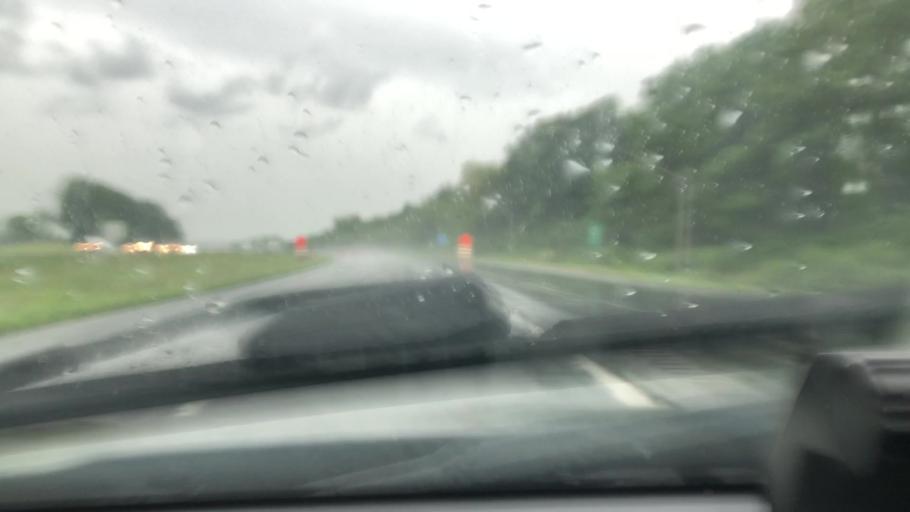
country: US
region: Pennsylvania
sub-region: Northampton County
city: Nazareth
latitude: 40.7141
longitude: -75.2902
